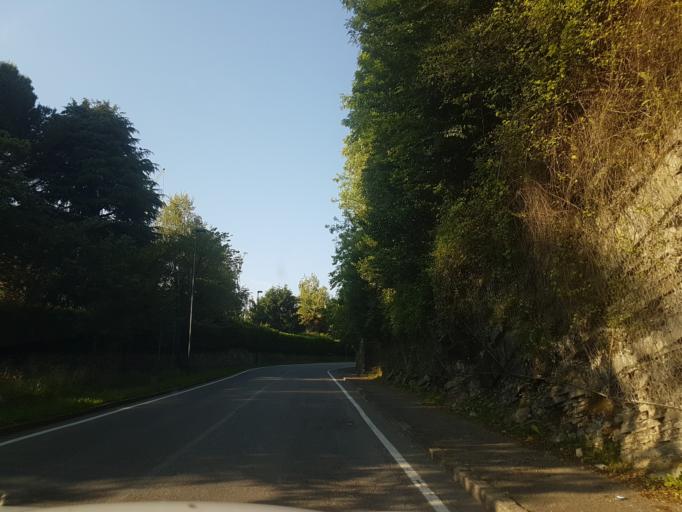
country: IT
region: Lombardy
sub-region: Provincia di Lecco
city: Oggiono
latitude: 45.7936
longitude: 9.3537
